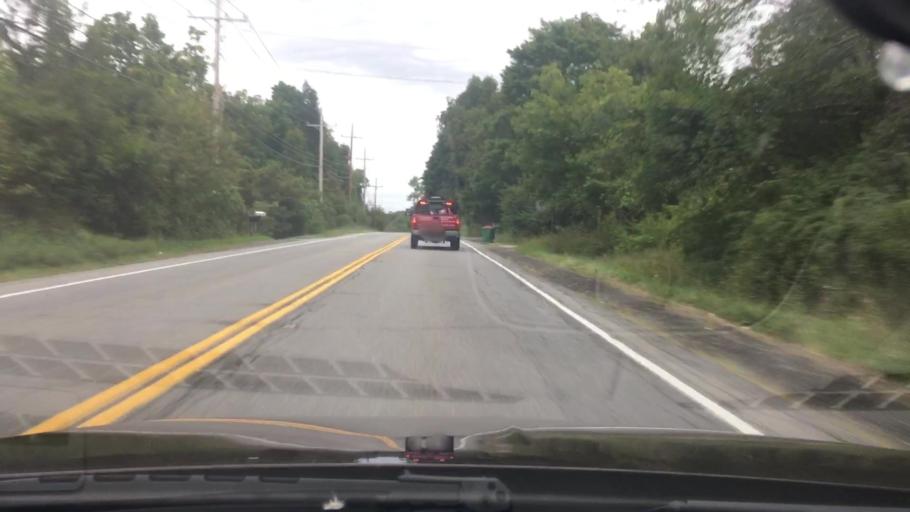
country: US
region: New York
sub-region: Dutchess County
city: Pleasant Valley
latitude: 41.7616
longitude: -73.7824
